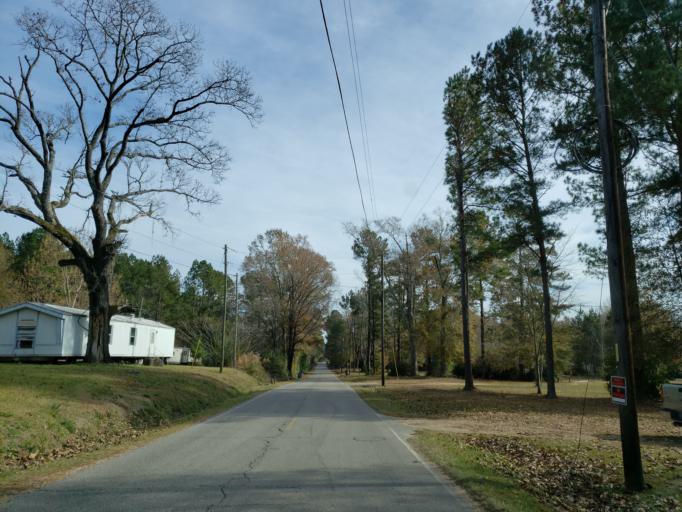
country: US
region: Mississippi
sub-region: Forrest County
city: Rawls Springs
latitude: 31.3964
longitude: -89.3885
